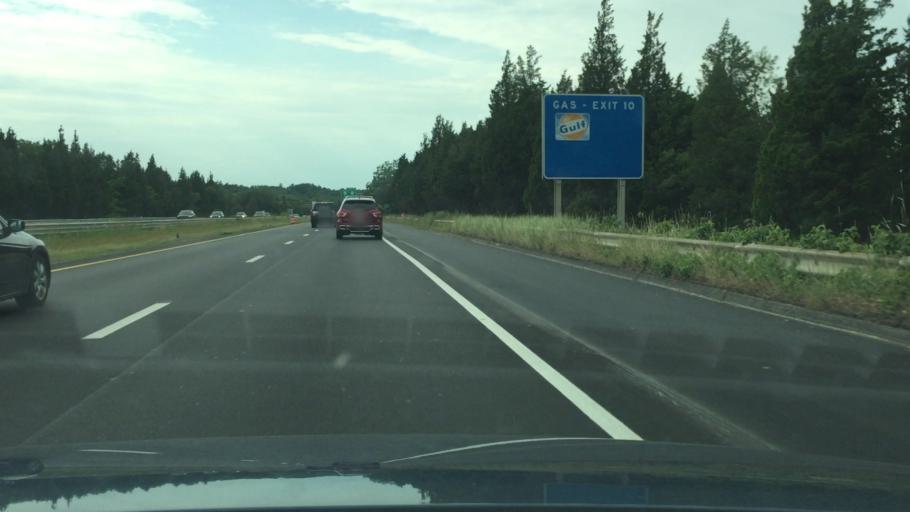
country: US
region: Massachusetts
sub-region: Plymouth County
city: Kingston
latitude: 41.9953
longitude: -70.7199
